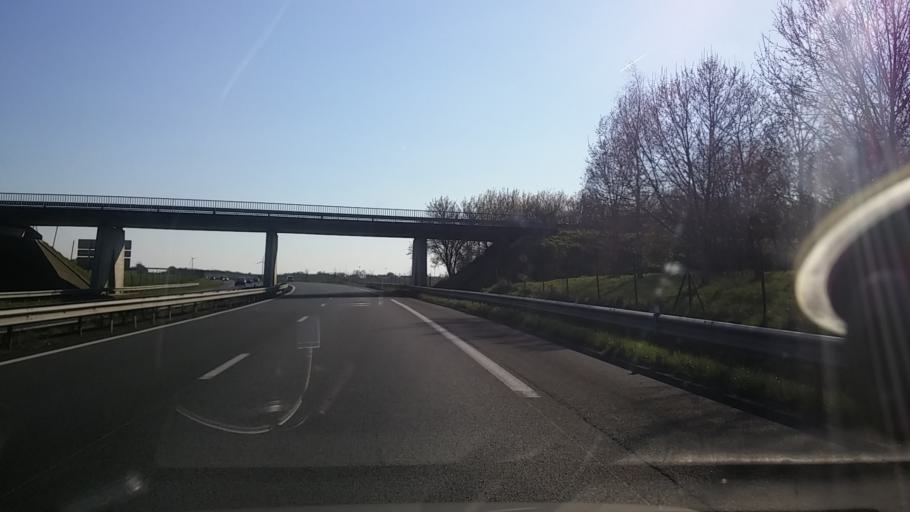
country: FR
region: Centre
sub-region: Departement de l'Indre
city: Vatan
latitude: 47.0815
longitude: 1.8279
